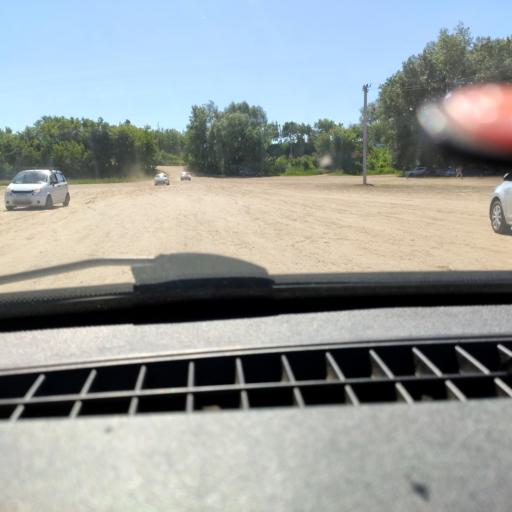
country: RU
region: Bashkortostan
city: Ufa
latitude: 54.7065
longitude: 55.9559
